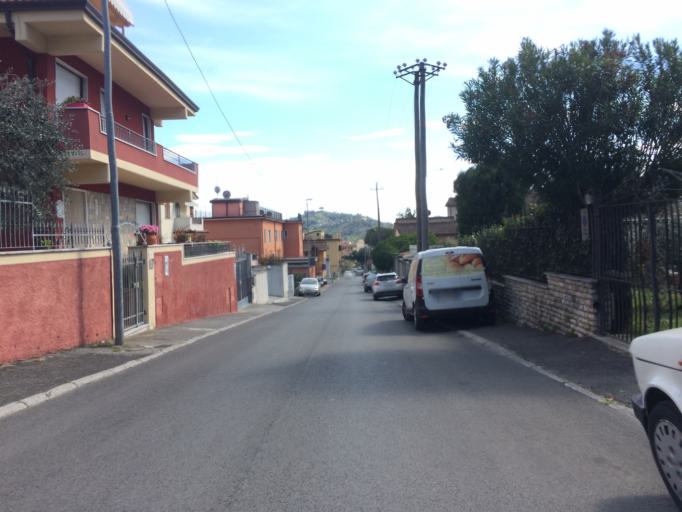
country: IT
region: Tuscany
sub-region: Provincia di Massa-Carrara
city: Carrara
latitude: 44.0719
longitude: 10.0768
